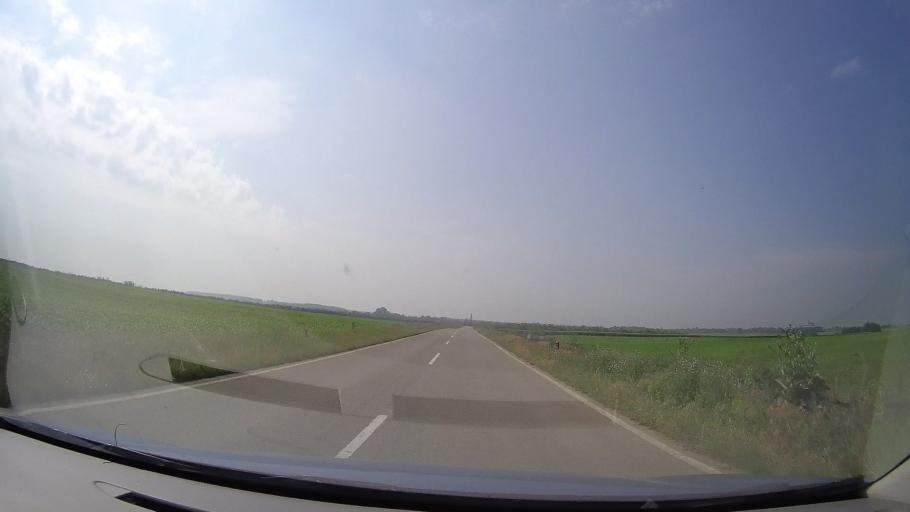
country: RS
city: Jasa Tomic
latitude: 45.4646
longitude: 20.8523
